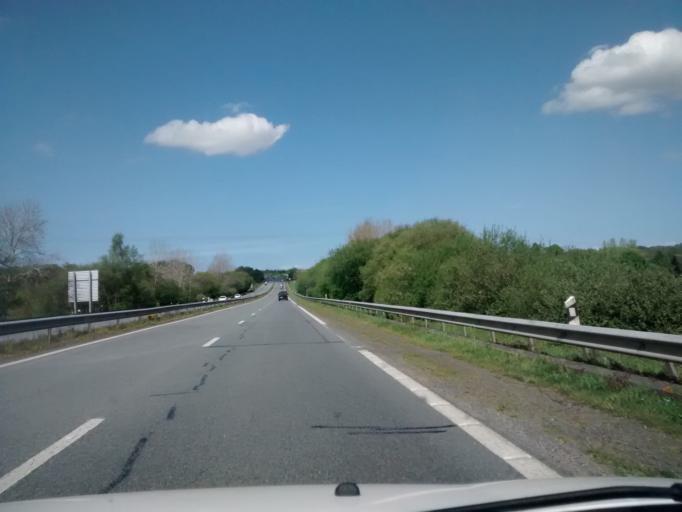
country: FR
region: Brittany
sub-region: Departement des Cotes-d'Armor
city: Saint-Samson-sur-Rance
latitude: 48.4963
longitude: -2.0406
